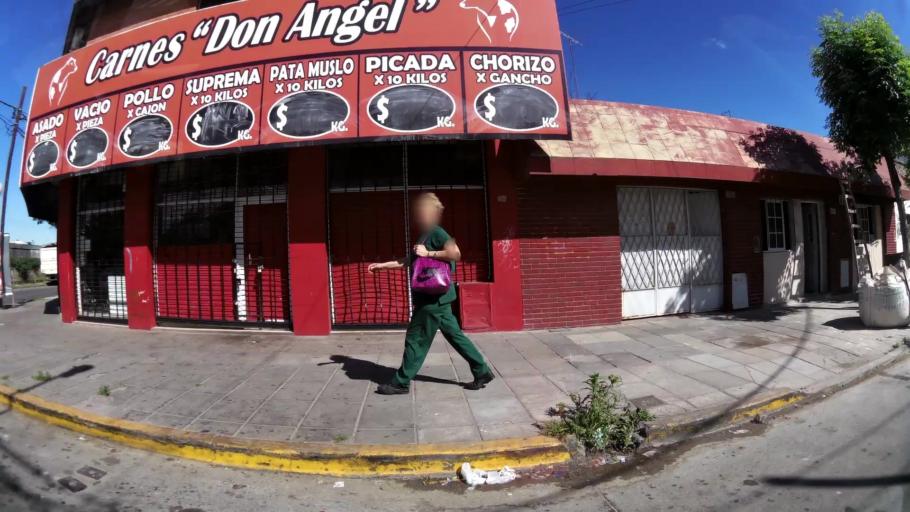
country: AR
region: Buenos Aires
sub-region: Partido de San Isidro
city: San Isidro
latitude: -34.5081
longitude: -58.5671
